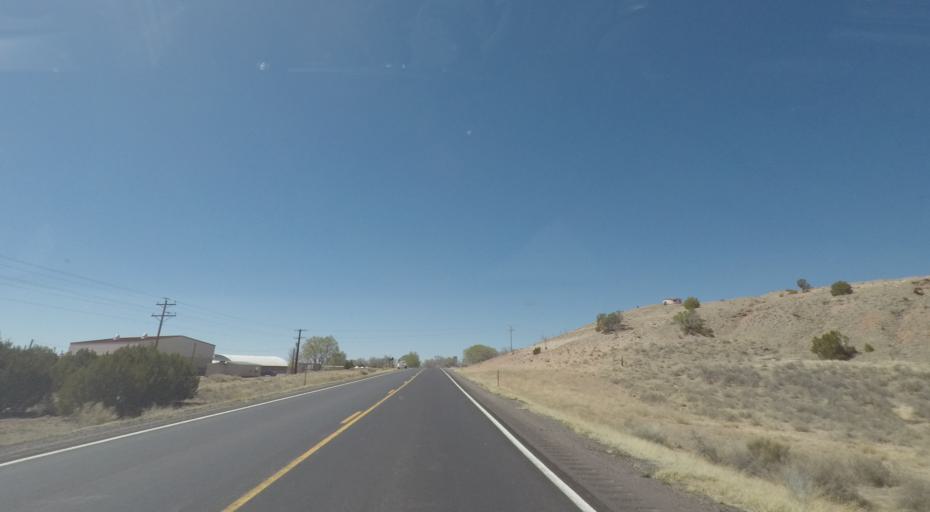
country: US
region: New Mexico
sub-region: Catron County
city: Reserve
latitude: 34.3394
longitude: -108.4897
